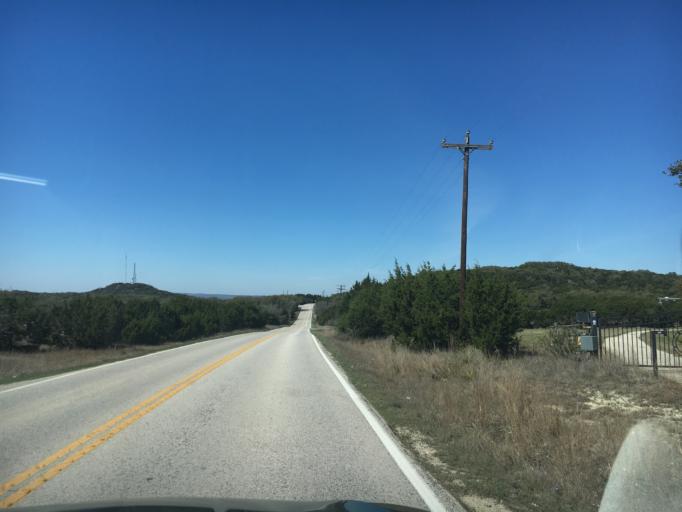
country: US
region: Texas
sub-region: Hays County
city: Dripping Springs
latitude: 30.2957
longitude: -98.0862
